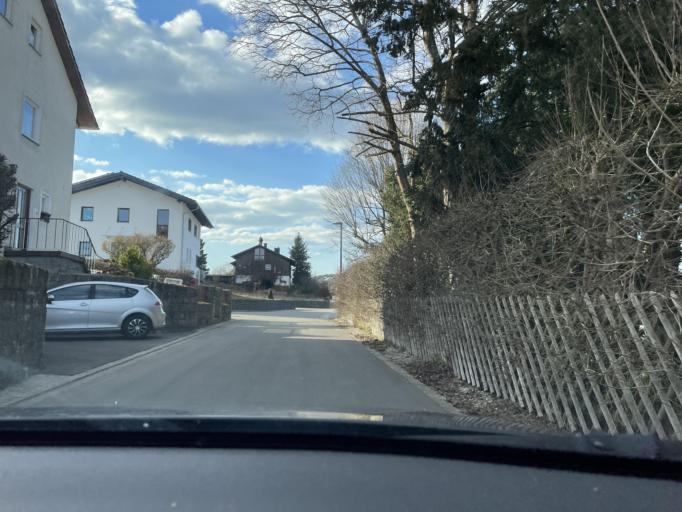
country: DE
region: Bavaria
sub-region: Lower Bavaria
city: Viechtach
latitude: 49.0780
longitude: 12.8801
